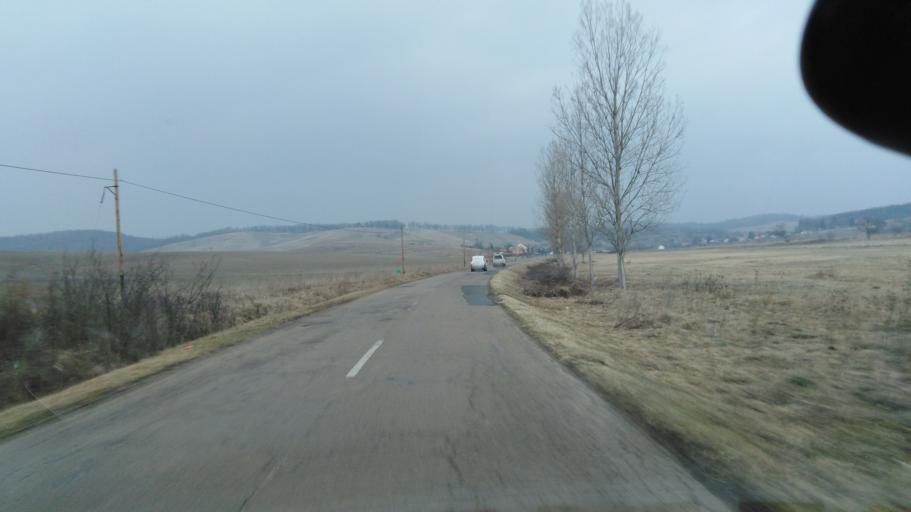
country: HU
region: Nograd
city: Tar
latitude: 48.0310
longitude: 19.7173
